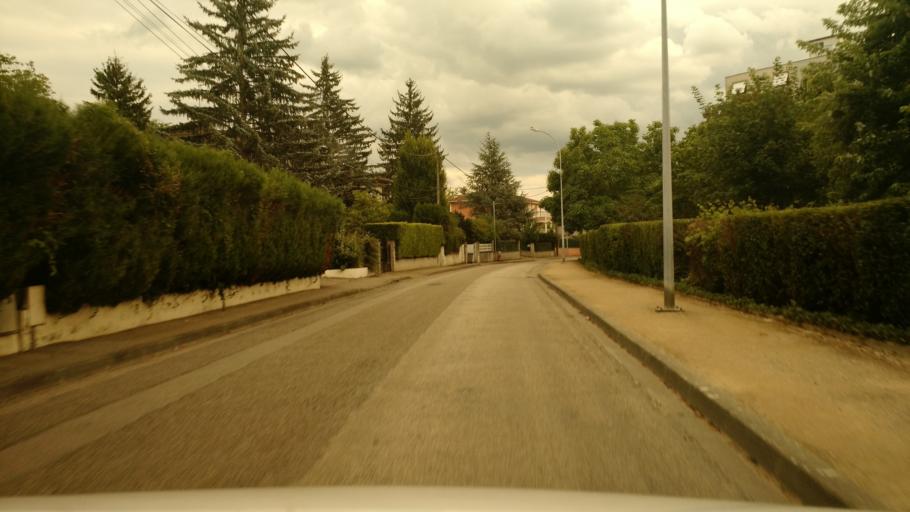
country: FR
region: Rhone-Alpes
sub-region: Departement de l'Ain
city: Montluel
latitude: 45.8528
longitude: 5.0608
